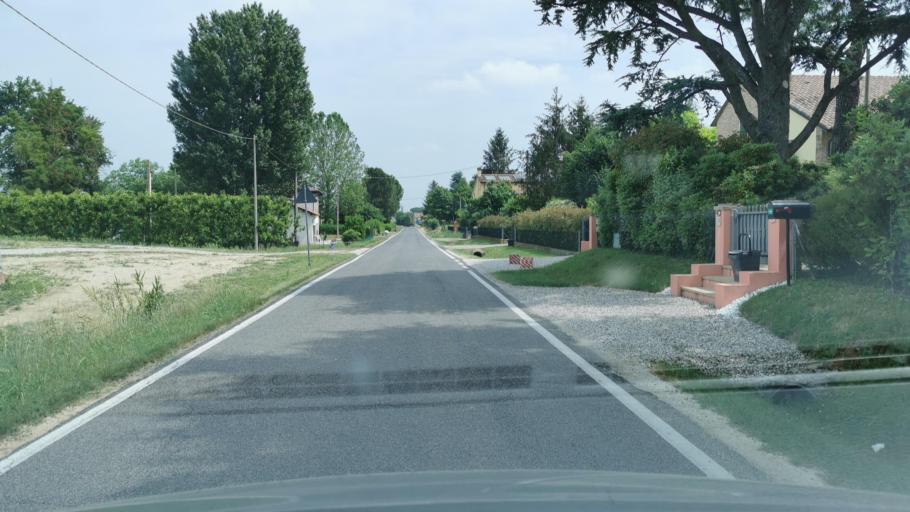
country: IT
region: Emilia-Romagna
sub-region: Provincia di Ravenna
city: Russi
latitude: 44.3981
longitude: 12.0183
